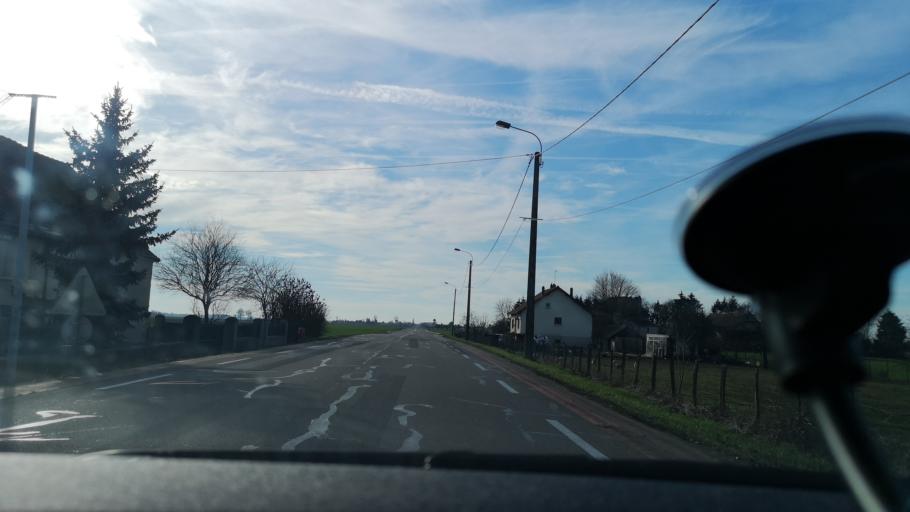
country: FR
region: Franche-Comte
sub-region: Departement du Jura
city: Petit-Noir
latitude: 46.9789
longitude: 5.3153
